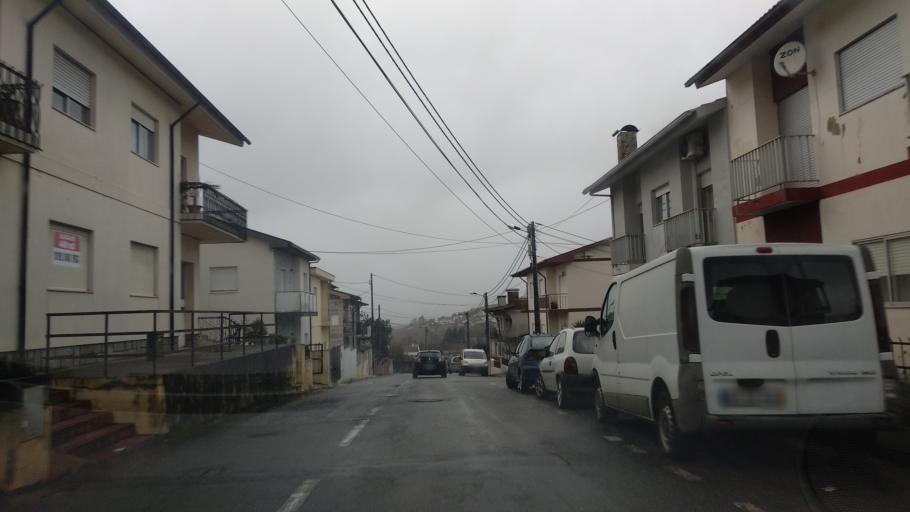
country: PT
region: Braga
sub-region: Braga
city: Braga
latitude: 41.5274
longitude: -8.4407
